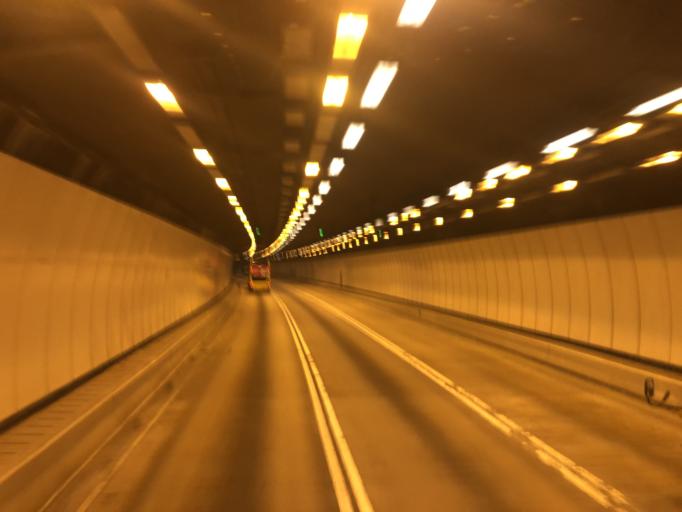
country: HK
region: Yuen Long
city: Yuen Long Kau Hui
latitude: 22.4080
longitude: 114.0600
